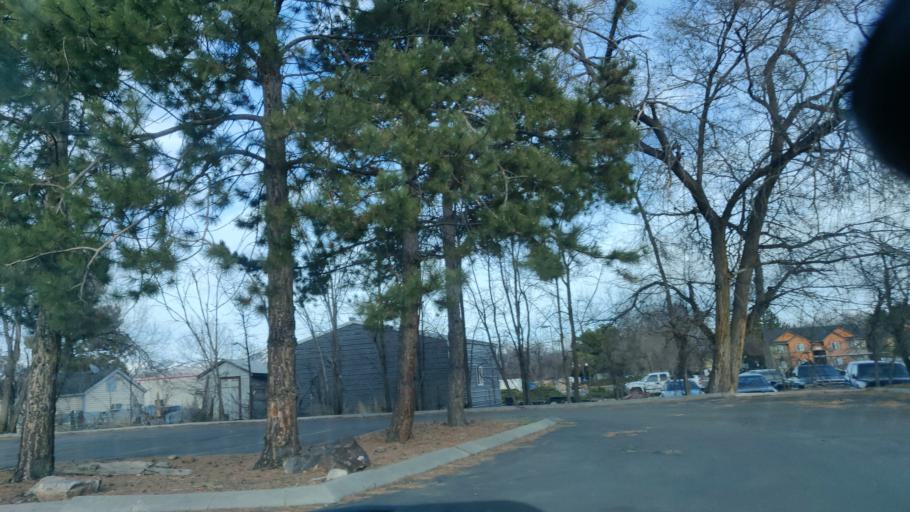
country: US
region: Idaho
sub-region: Ada County
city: Garden City
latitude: 43.6182
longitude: -116.2657
